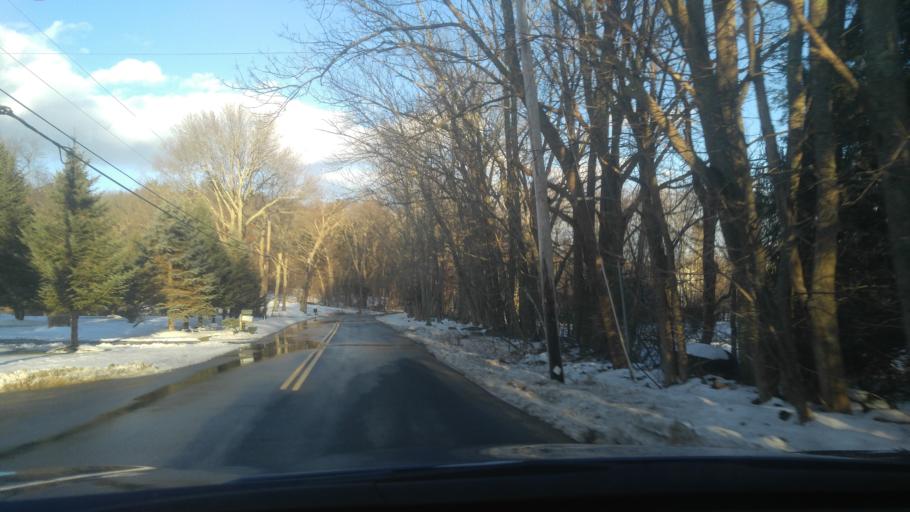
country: US
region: Rhode Island
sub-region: Kent County
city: Coventry
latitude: 41.7192
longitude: -71.6593
